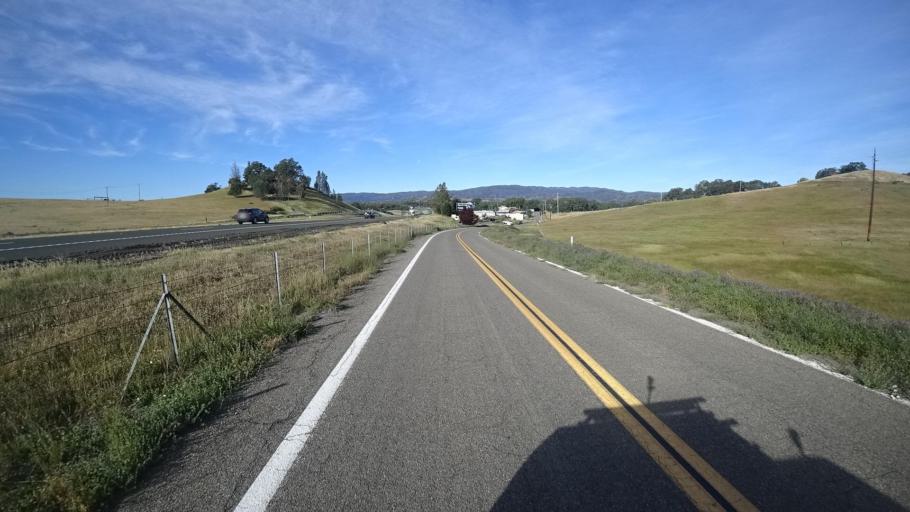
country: US
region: California
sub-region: Lake County
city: North Lakeport
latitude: 39.0883
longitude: -122.9206
